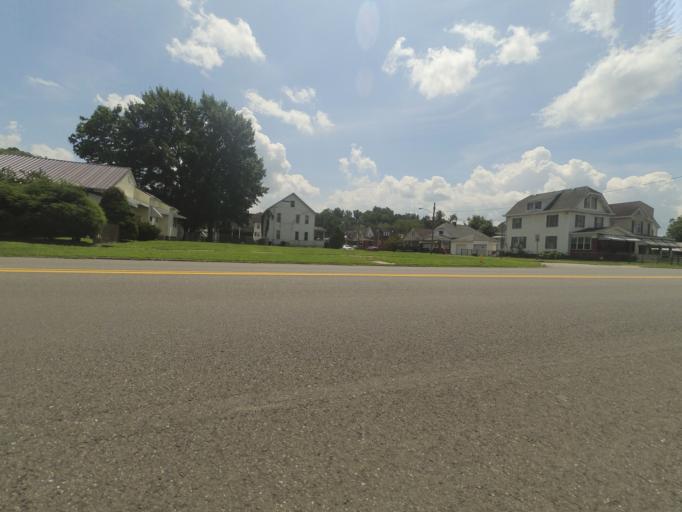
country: US
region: West Virginia
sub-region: Cabell County
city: Huntington
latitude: 38.4203
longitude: -82.4124
